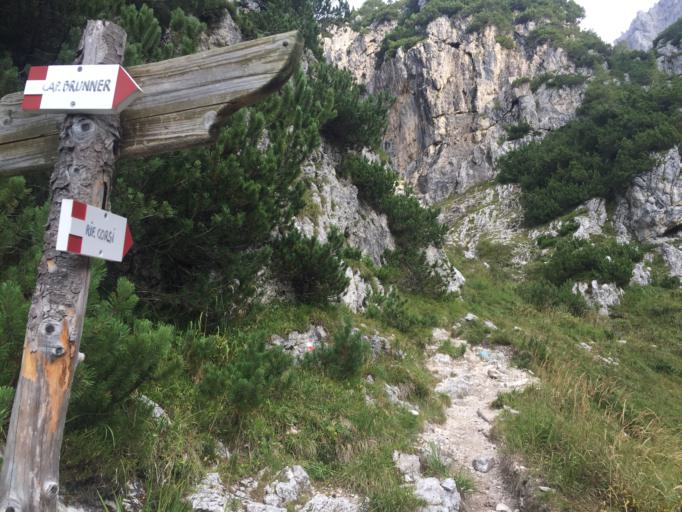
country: SI
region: Bovec
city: Bovec
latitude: 46.4208
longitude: 13.5024
